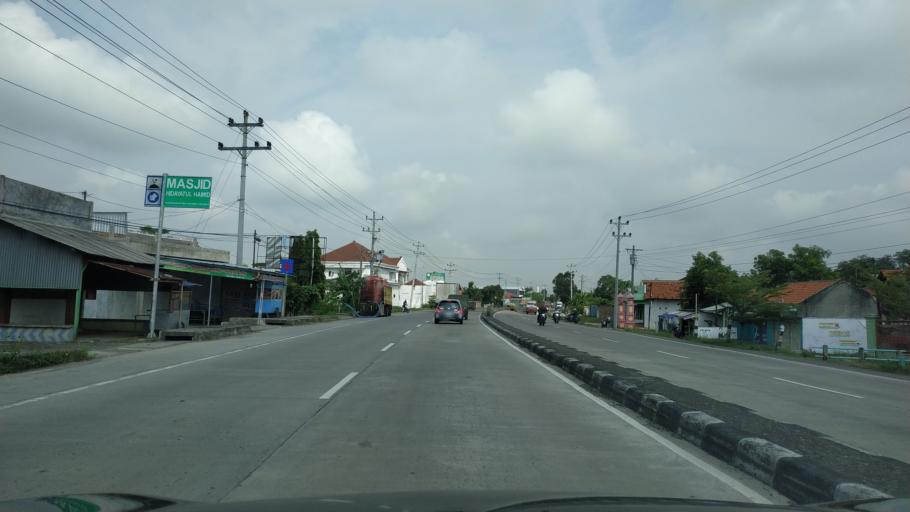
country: ID
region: Central Java
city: Bulakamba
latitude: -6.8740
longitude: 108.9406
